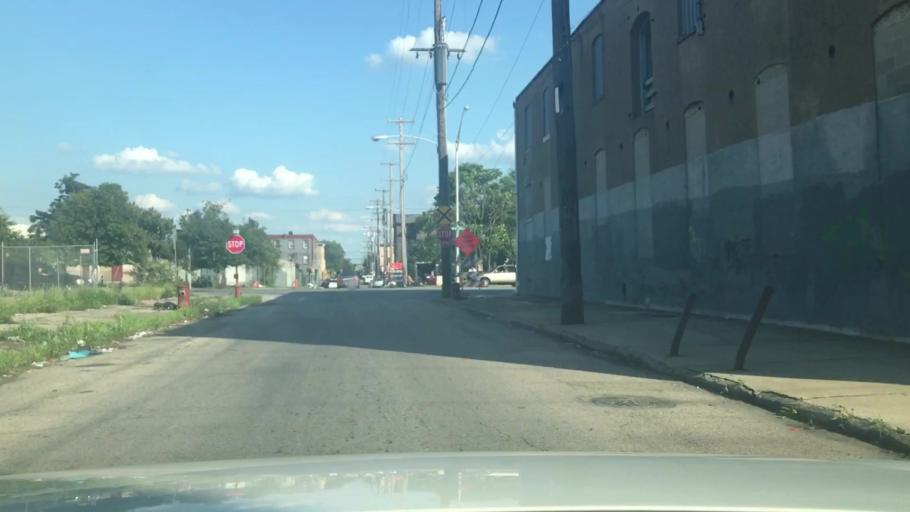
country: US
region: Pennsylvania
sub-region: Philadelphia County
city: Philadelphia
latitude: 39.9886
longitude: -75.1375
